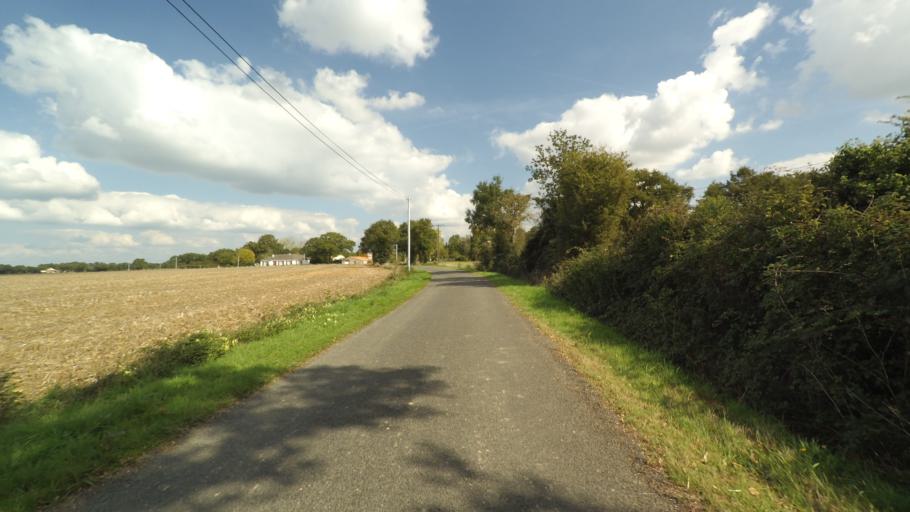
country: FR
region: Pays de la Loire
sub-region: Departement de la Vendee
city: Bouffere
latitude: 46.9636
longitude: -1.3767
